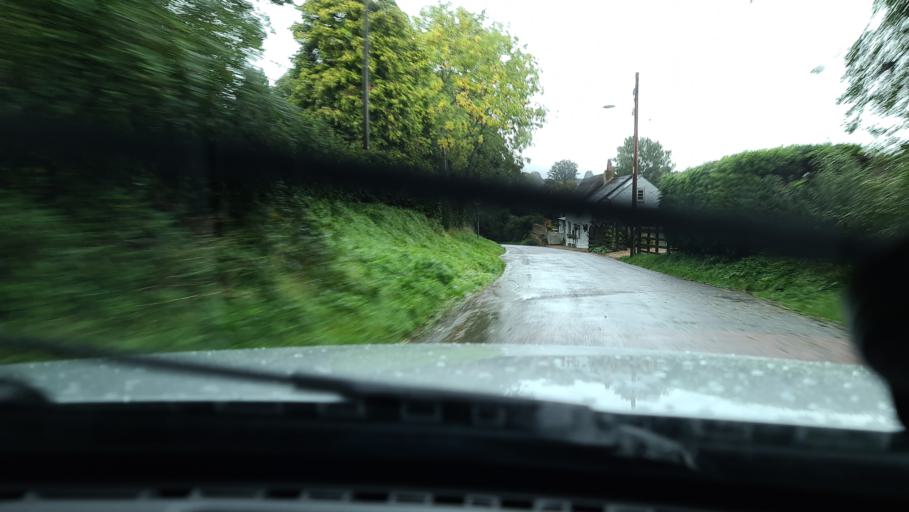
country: GB
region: England
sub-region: Oxfordshire
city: Deddington
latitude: 51.9258
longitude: -1.3681
